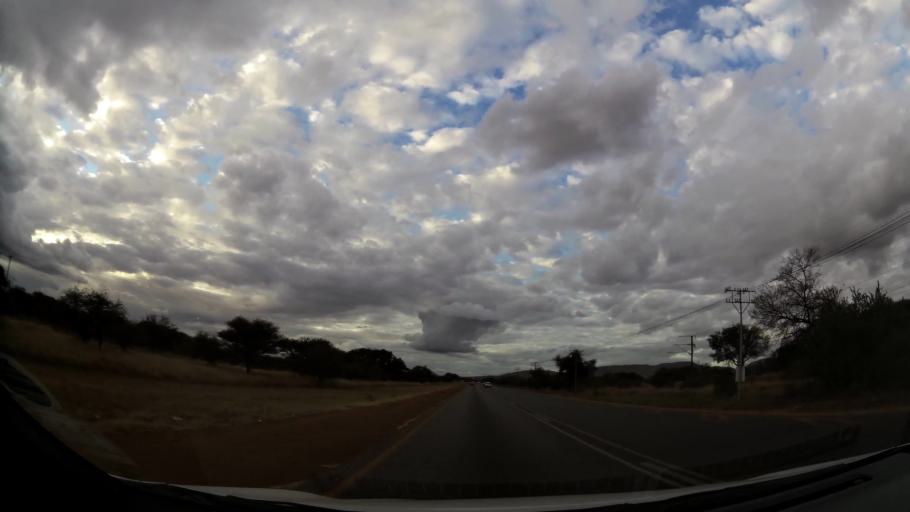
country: ZA
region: Limpopo
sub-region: Waterberg District Municipality
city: Mokopane
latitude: -24.2261
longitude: 29.0015
